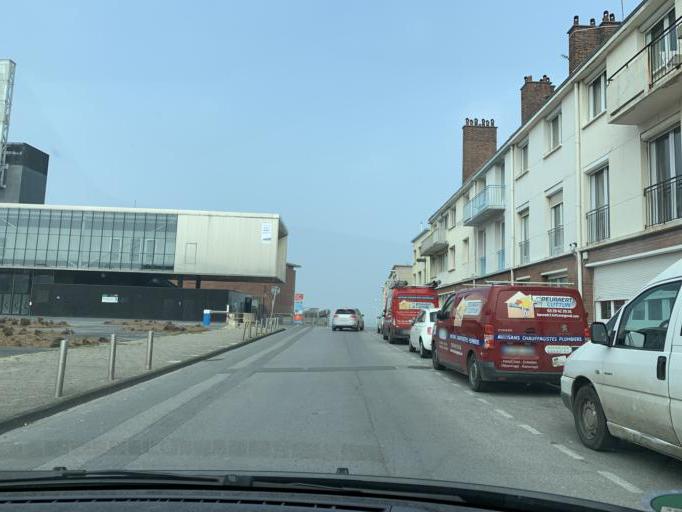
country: FR
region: Nord-Pas-de-Calais
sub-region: Departement du Nord
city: Dunkerque
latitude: 51.0486
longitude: 2.3901
